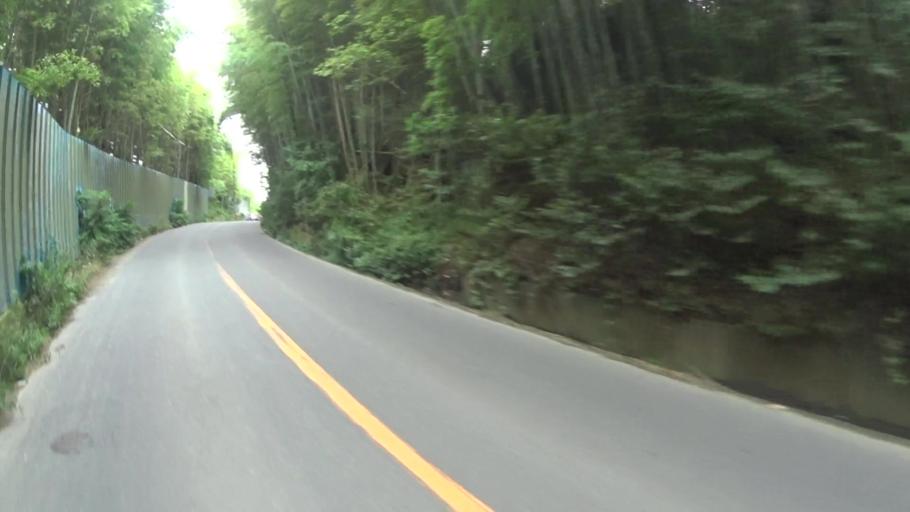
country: JP
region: Kyoto
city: Tanabe
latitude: 34.7941
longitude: 135.7426
